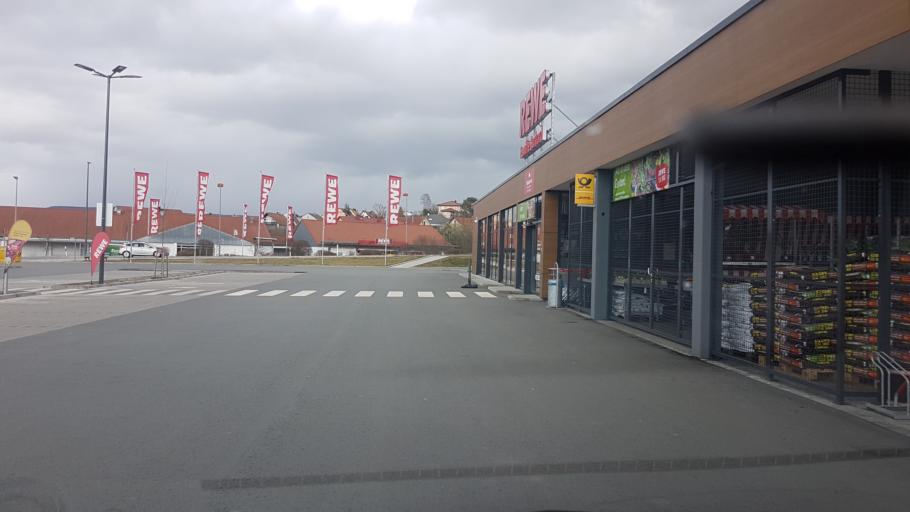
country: DE
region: Bavaria
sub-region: Upper Franconia
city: Hirschaid
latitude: 49.8051
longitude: 10.9695
